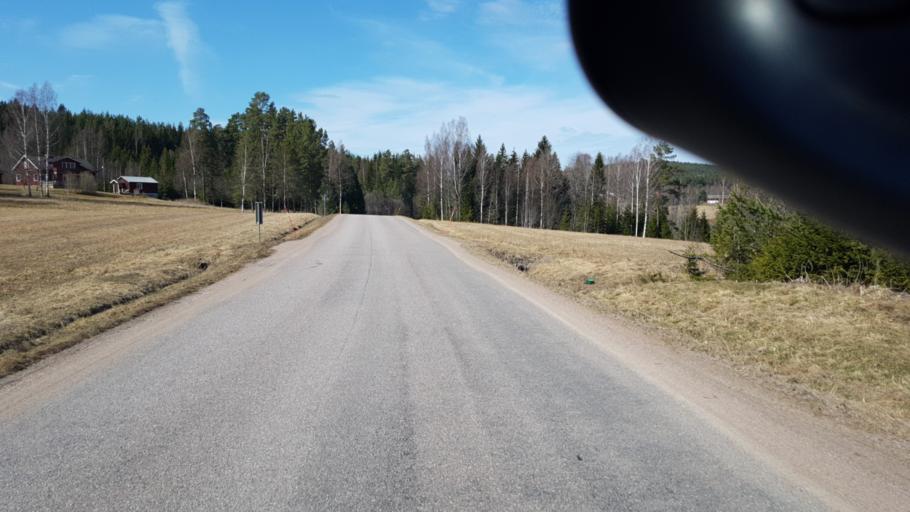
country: SE
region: Vaermland
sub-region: Arvika Kommun
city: Arvika
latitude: 59.6284
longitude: 12.8016
